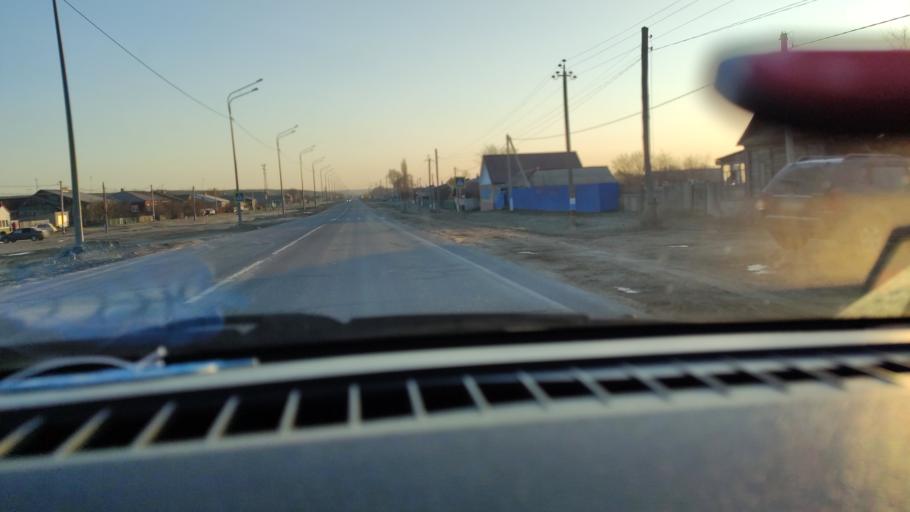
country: RU
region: Saratov
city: Sinodskoye
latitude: 51.9909
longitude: 46.6684
